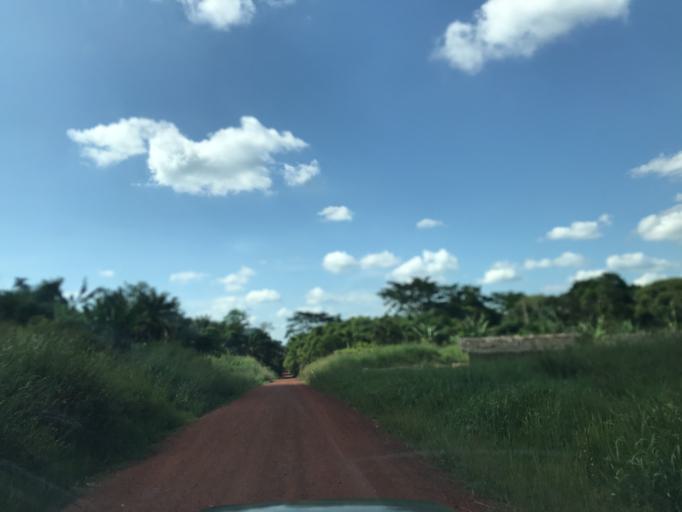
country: CD
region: Eastern Province
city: Kisangani
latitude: 1.2331
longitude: 25.2710
